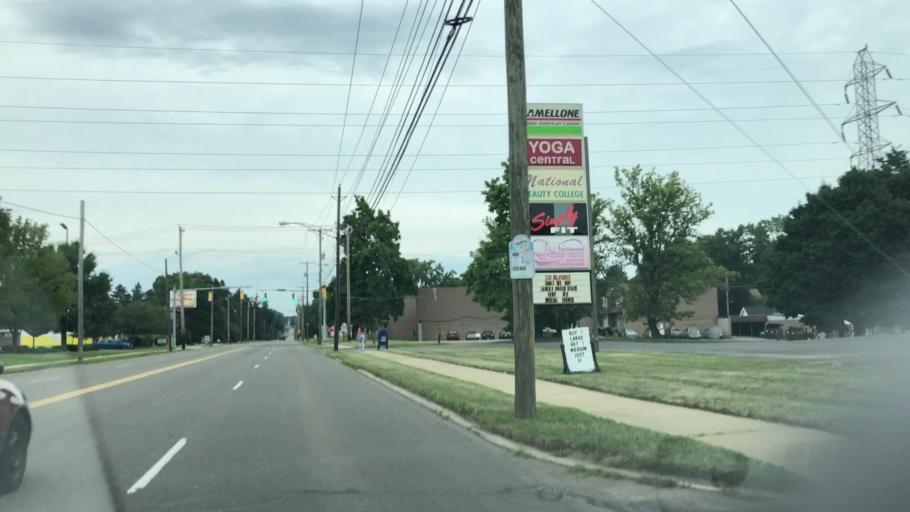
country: US
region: Ohio
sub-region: Stark County
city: North Canton
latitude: 40.8492
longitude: -81.3927
